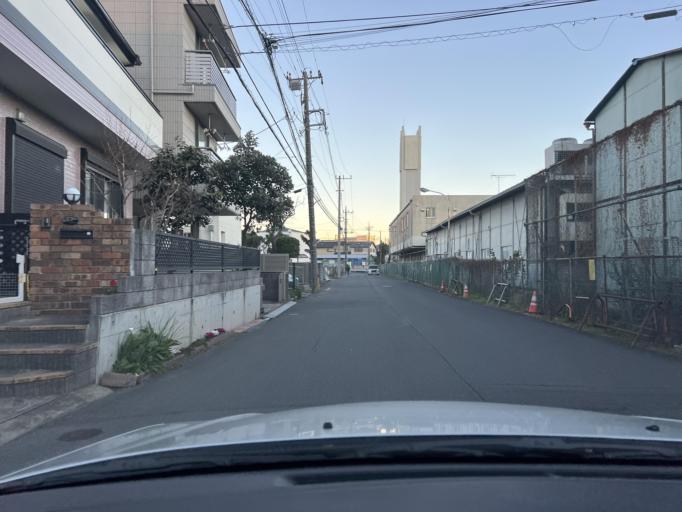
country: JP
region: Chiba
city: Kashiwa
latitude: 35.8956
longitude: 139.9606
